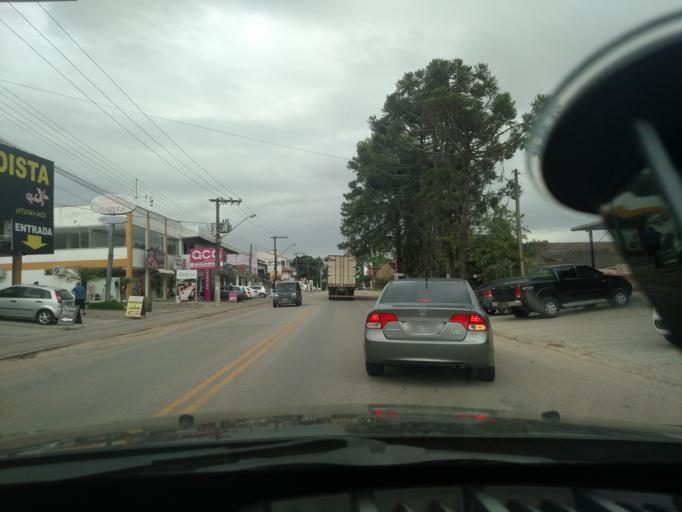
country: BR
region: Santa Catarina
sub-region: Gaspar
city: Gaspar
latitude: -26.9036
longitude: -48.8322
